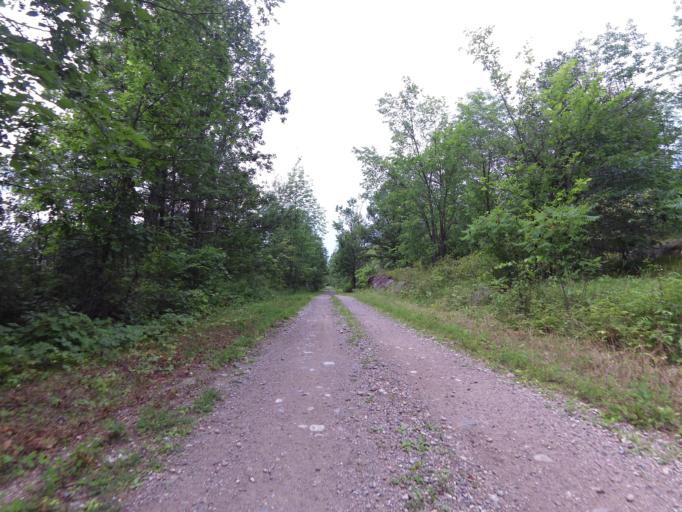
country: CA
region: Ontario
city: Perth
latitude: 44.8243
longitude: -76.5677
